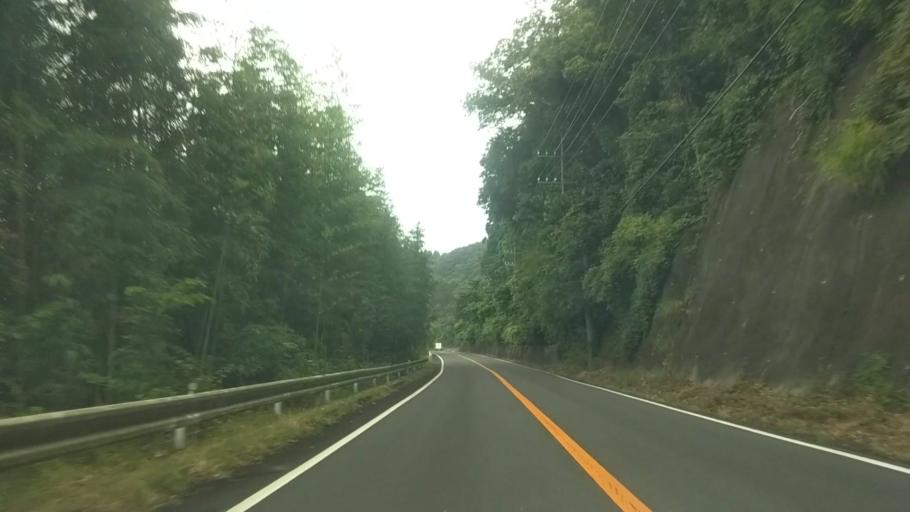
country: JP
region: Chiba
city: Kawaguchi
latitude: 35.2368
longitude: 140.0745
